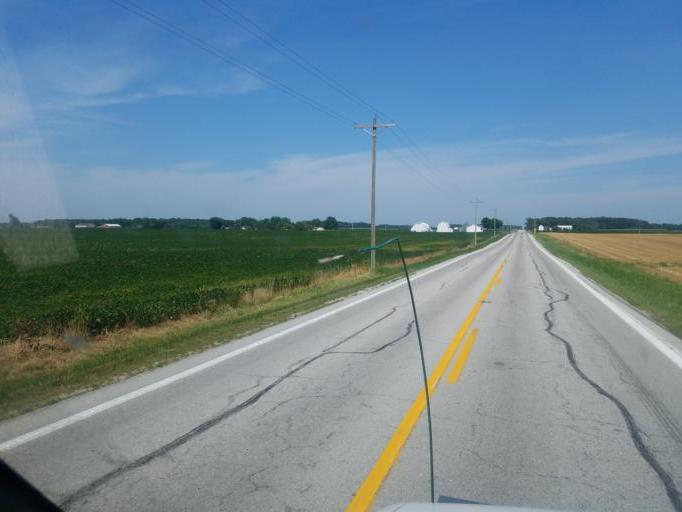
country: US
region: Ohio
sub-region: Shelby County
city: Botkins
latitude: 40.4968
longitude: -84.2158
